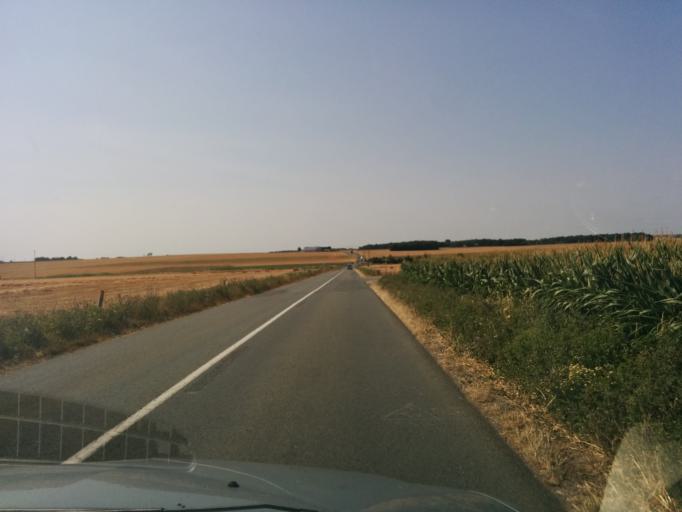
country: FR
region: Poitou-Charentes
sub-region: Departement de la Vienne
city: Mirebeau
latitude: 46.7308
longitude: 0.1947
